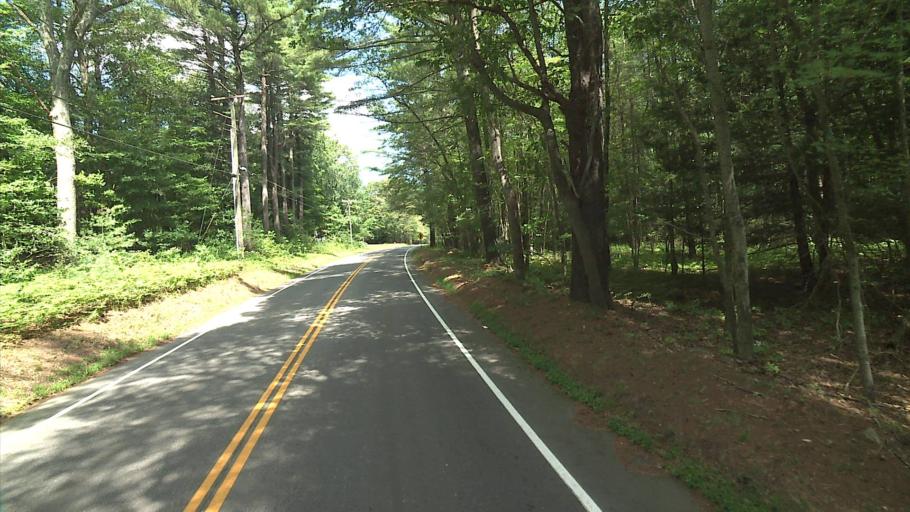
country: US
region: Connecticut
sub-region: Windham County
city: South Woodstock
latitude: 41.9574
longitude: -72.0786
